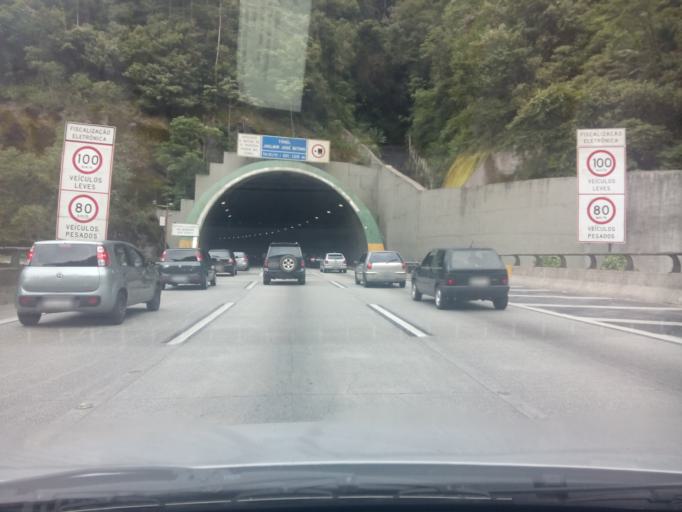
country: BR
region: Sao Paulo
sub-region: Cubatao
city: Cubatao
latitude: -23.8866
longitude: -46.5006
